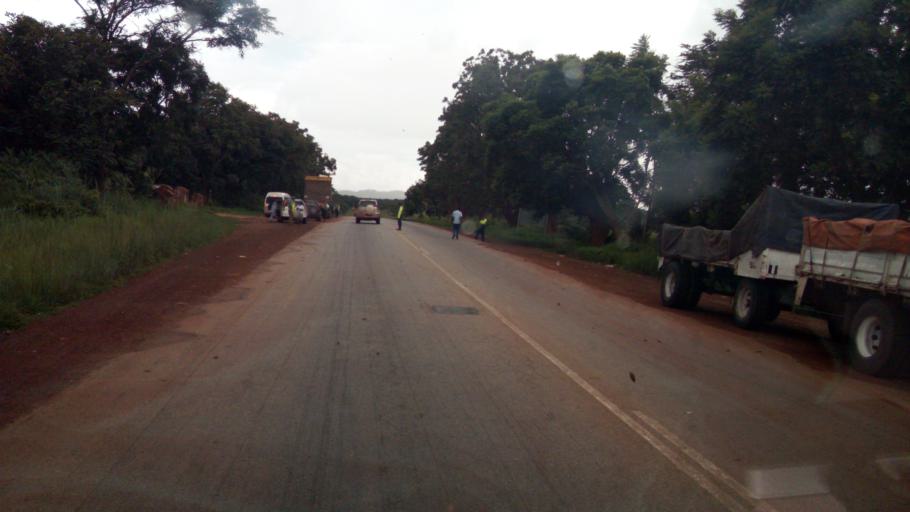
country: ZW
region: Mashonaland Central
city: Mazowe
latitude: -17.5819
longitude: 30.9700
